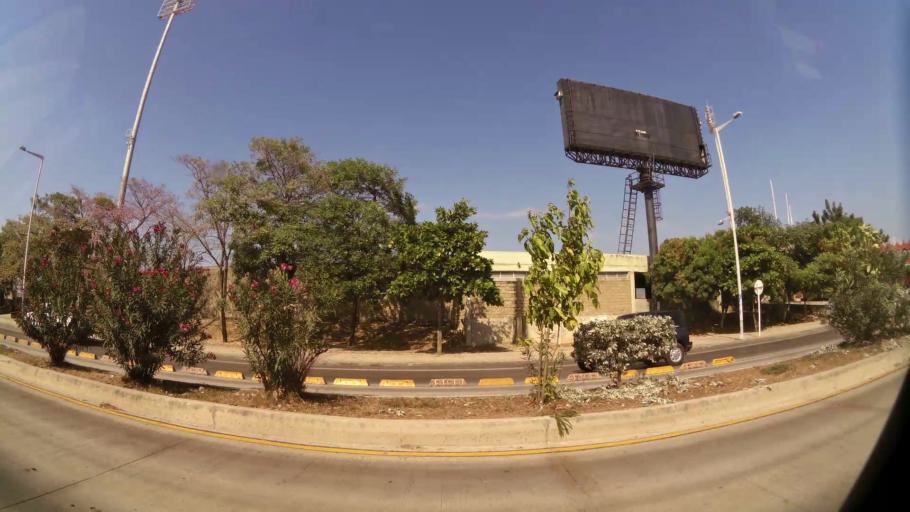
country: CO
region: Bolivar
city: Cartagena
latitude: 10.4045
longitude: -75.4987
